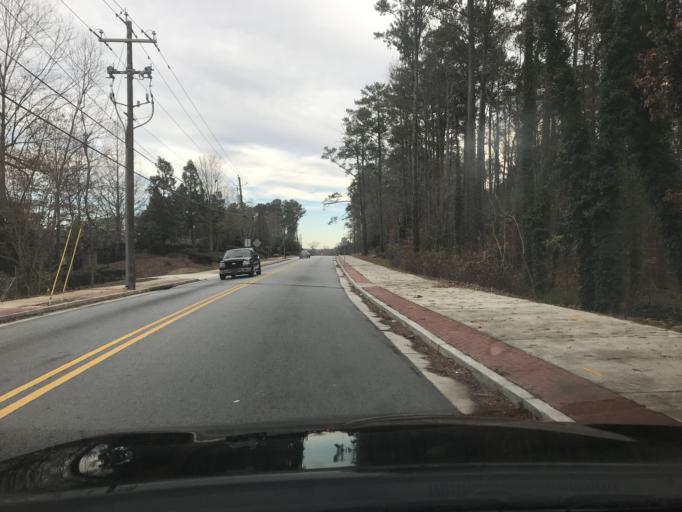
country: US
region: Georgia
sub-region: Fulton County
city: East Point
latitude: 33.7167
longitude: -84.5082
